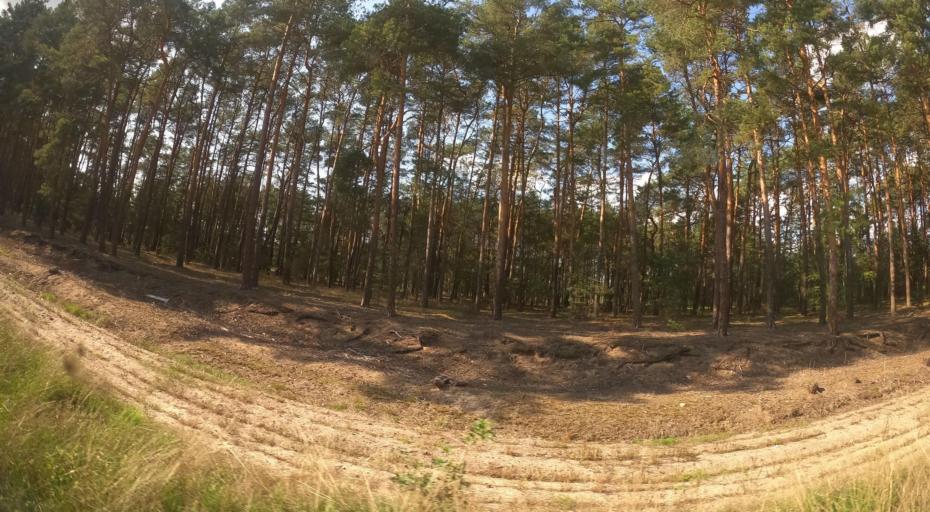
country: PL
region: Lubusz
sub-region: Powiat zielonogorski
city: Swidnica
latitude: 51.8675
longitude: 15.3146
